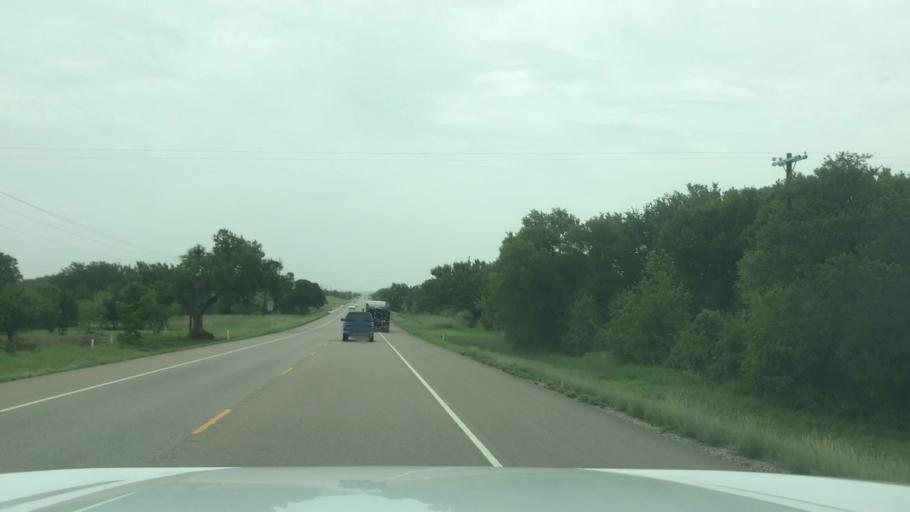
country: US
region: Texas
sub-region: Bosque County
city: Meridian
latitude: 31.9289
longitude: -97.6897
